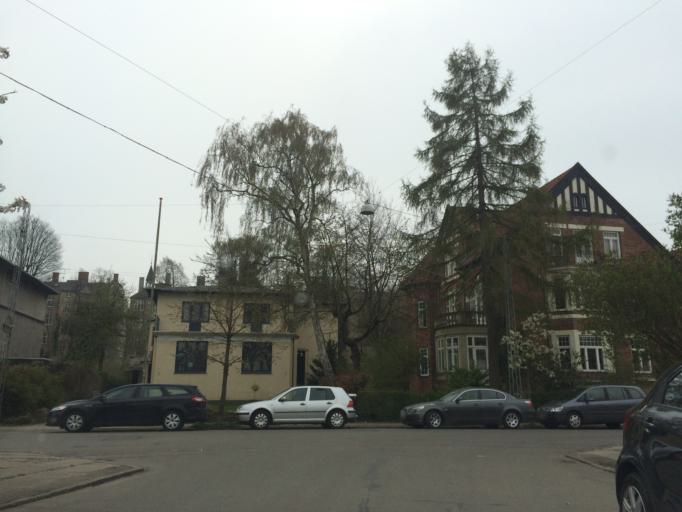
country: DK
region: Capital Region
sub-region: Frederiksberg Kommune
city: Frederiksberg
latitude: 55.6764
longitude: 12.5149
